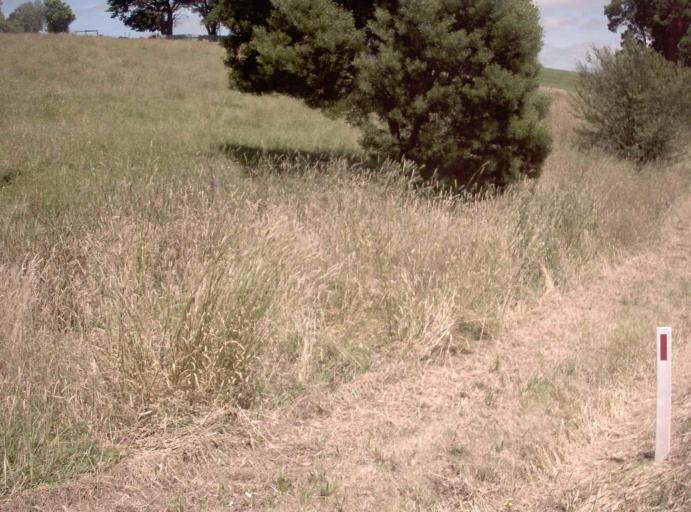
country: AU
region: Victoria
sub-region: Baw Baw
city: Warragul
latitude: -38.2939
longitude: 145.9020
